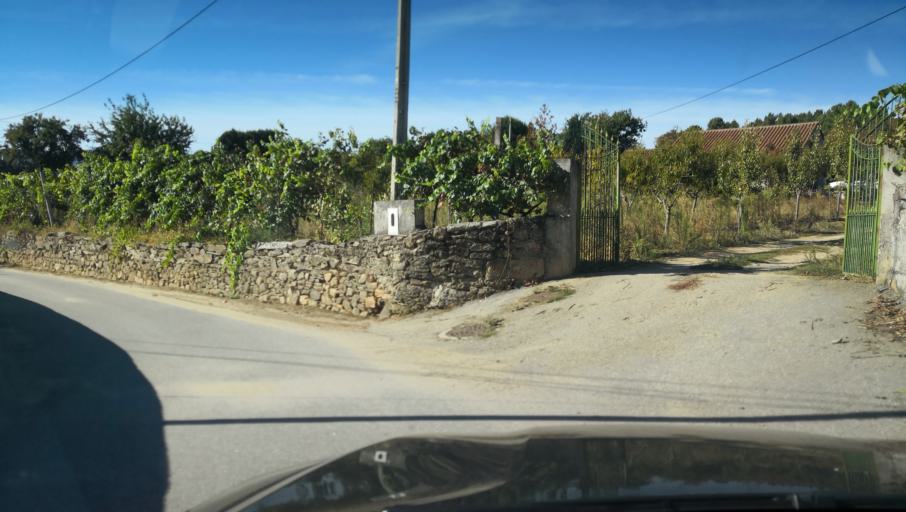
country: PT
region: Vila Real
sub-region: Vila Real
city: Vila Real
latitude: 41.2809
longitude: -7.7423
